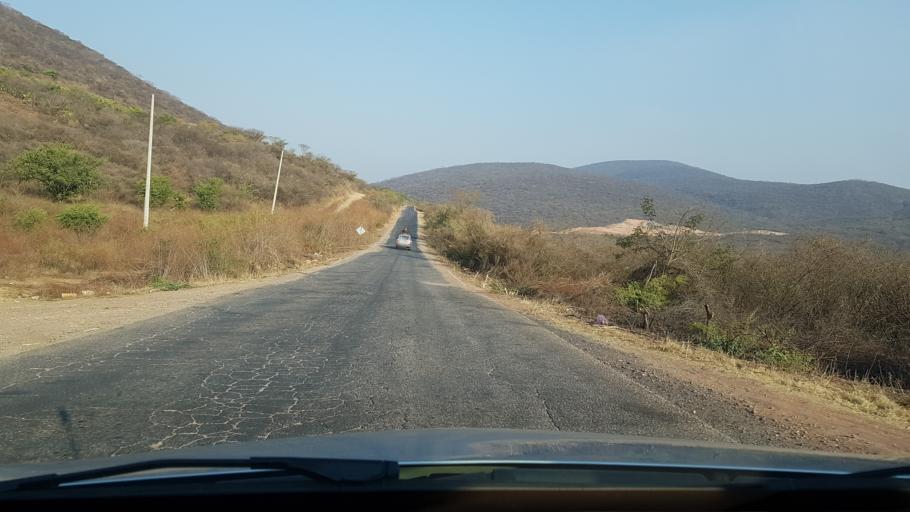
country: MX
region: Morelos
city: Tlaltizapan
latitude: 18.6707
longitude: -99.0546
